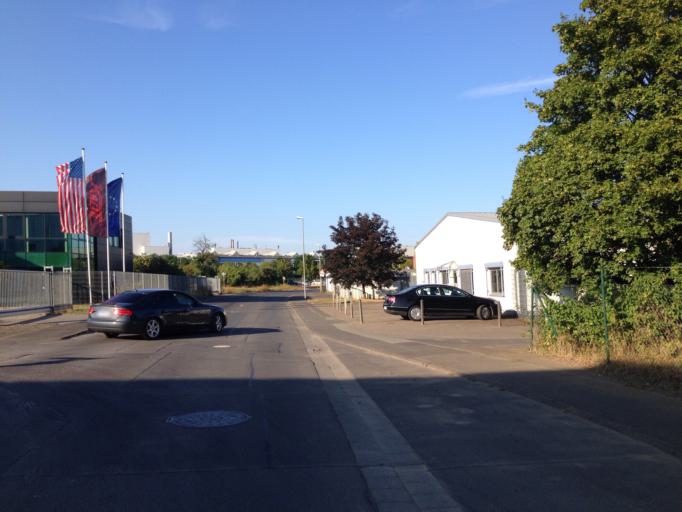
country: DE
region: Hesse
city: Lollar
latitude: 50.6471
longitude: 8.6981
